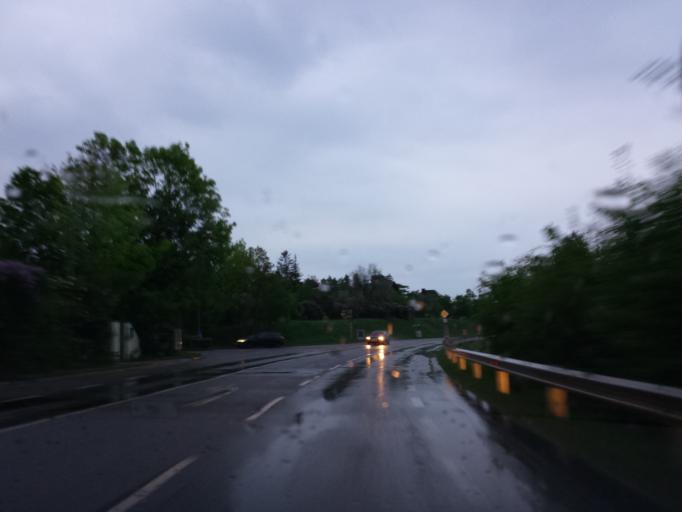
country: AT
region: Lower Austria
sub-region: Politischer Bezirk Modling
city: Perchtoldsdorf
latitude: 48.1296
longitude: 16.2600
